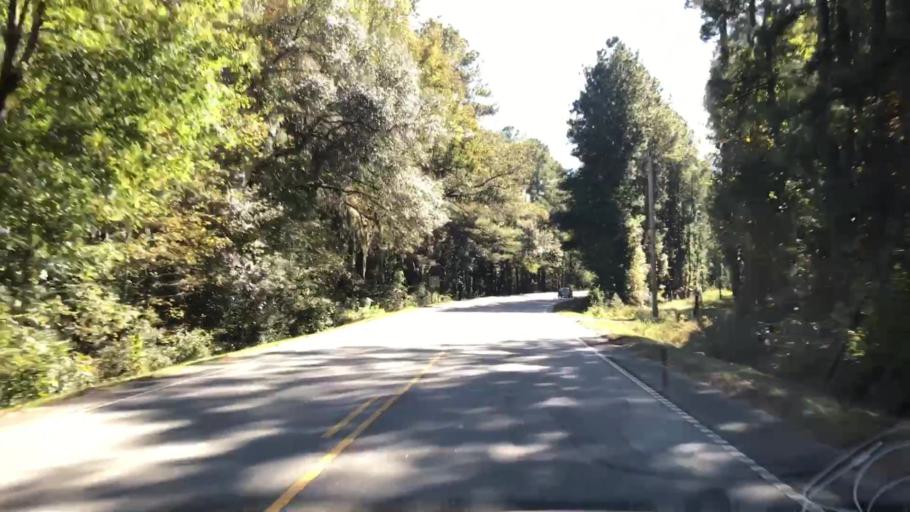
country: US
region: South Carolina
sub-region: Jasper County
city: Ridgeland
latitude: 32.5694
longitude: -80.9191
